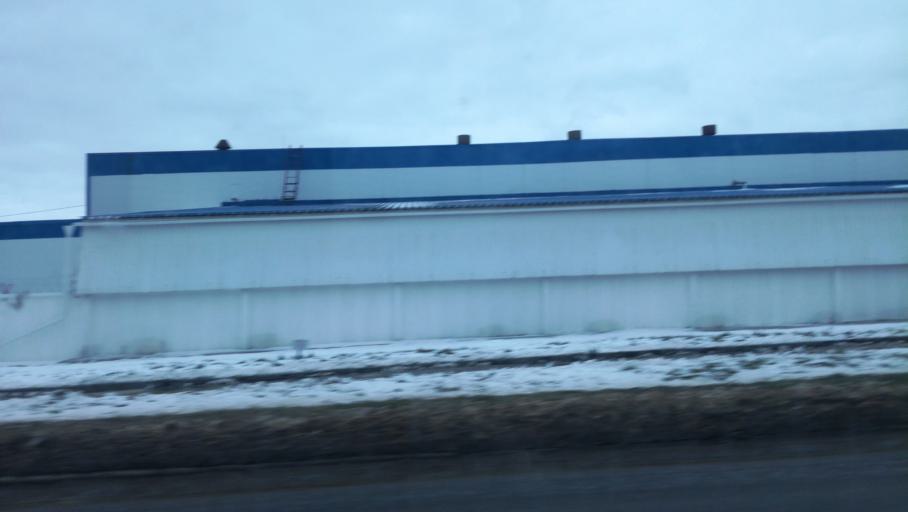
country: RU
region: Tula
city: Kosaya Gora
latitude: 54.1852
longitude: 37.5241
